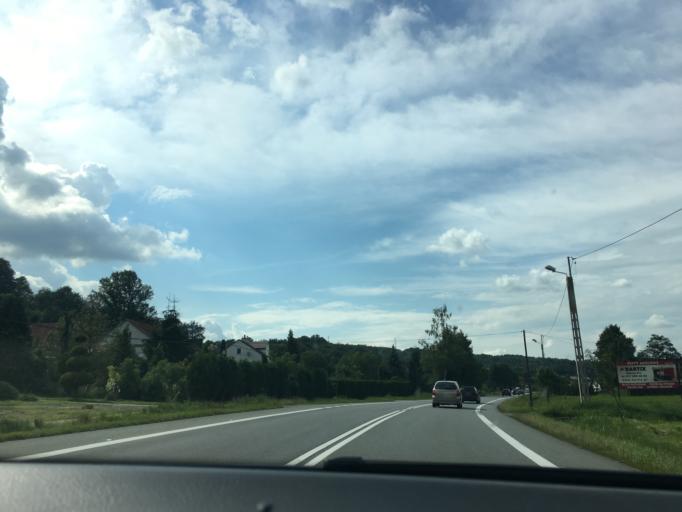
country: PL
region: Subcarpathian Voivodeship
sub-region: Powiat strzyzowski
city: Polomia
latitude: 49.9005
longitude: 21.8715
